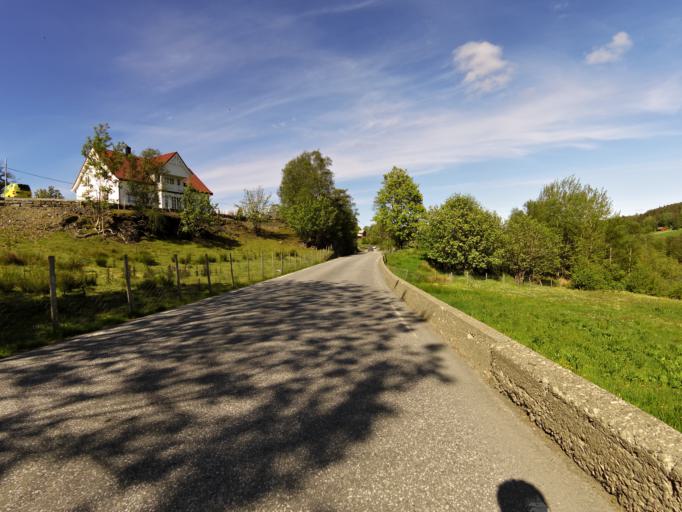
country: NO
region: Hordaland
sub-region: Stord
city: Leirvik
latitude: 59.7845
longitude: 5.4573
